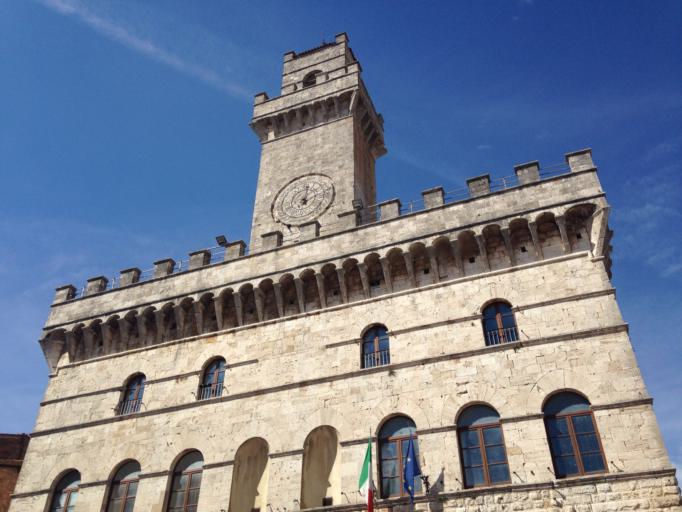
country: IT
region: Tuscany
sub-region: Provincia di Siena
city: Montepulciano
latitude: 43.0928
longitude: 11.7809
